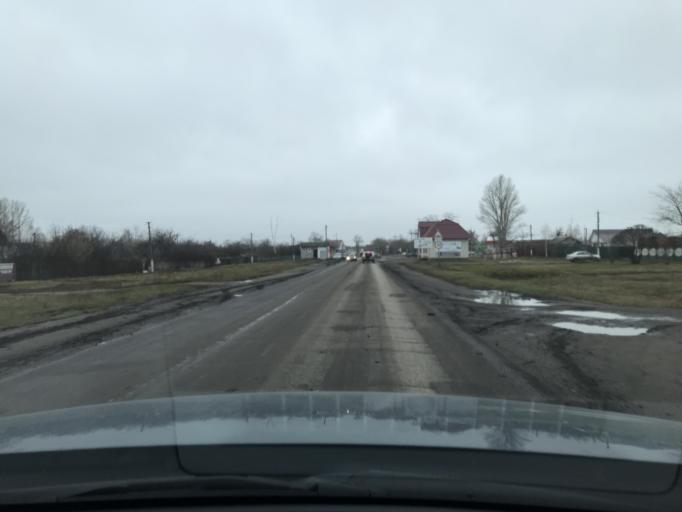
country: RU
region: Penza
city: Zemetchino
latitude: 53.5020
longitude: 42.6315
